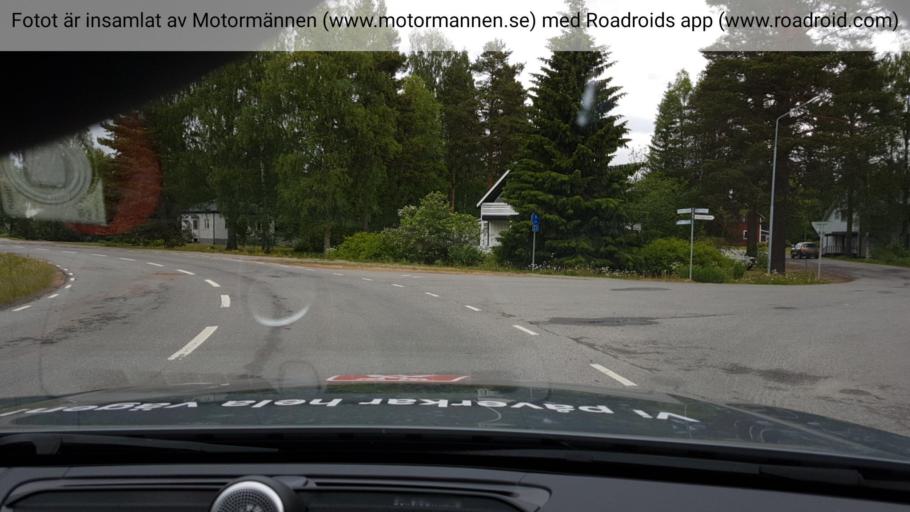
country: SE
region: Jaemtland
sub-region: Ragunda Kommun
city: Hammarstrand
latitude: 62.9836
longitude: 16.0906
